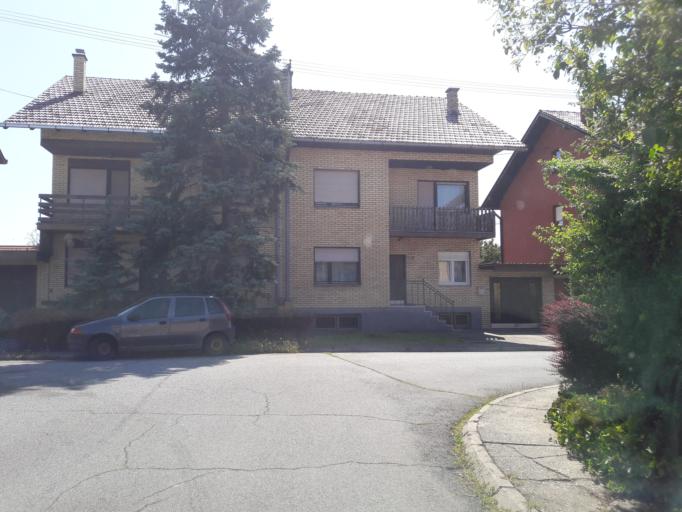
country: HR
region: Osjecko-Baranjska
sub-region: Grad Osijek
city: Osijek
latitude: 45.5576
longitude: 18.6573
